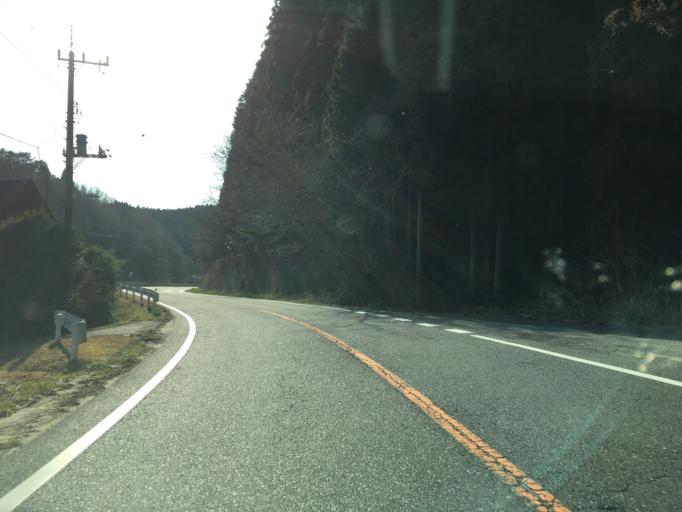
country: JP
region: Ibaraki
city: Takahagi
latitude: 36.7417
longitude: 140.5790
